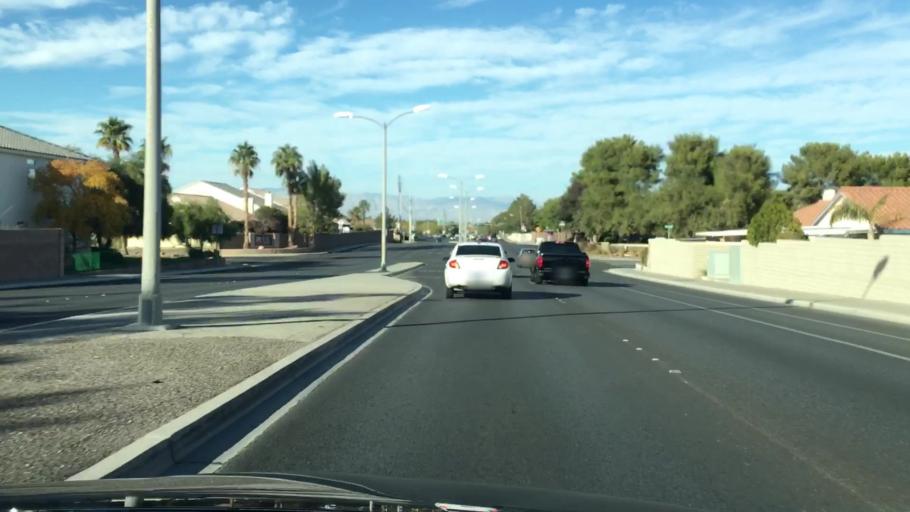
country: US
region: Nevada
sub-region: Clark County
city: Whitney
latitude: 36.0532
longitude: -115.1003
